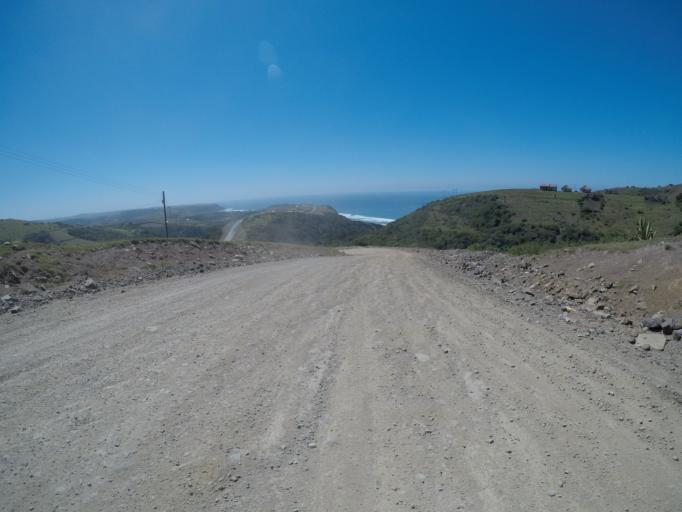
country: ZA
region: Eastern Cape
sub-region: OR Tambo District Municipality
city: Libode
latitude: -31.9950
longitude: 29.1292
